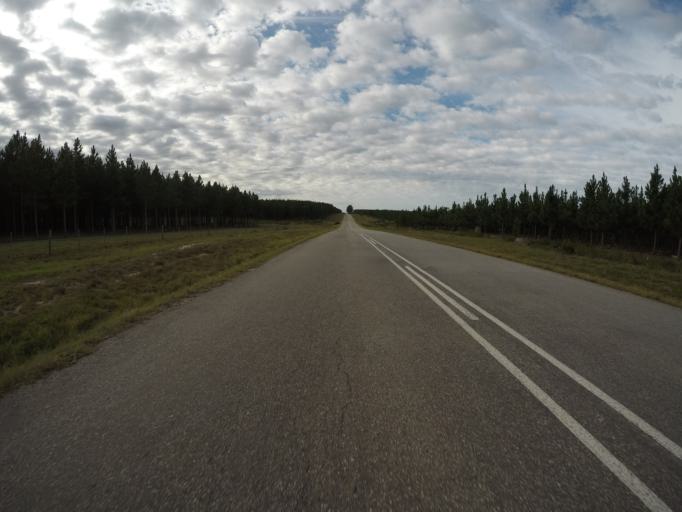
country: ZA
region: Eastern Cape
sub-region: Cacadu District Municipality
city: Kareedouw
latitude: -34.0254
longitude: 24.3675
